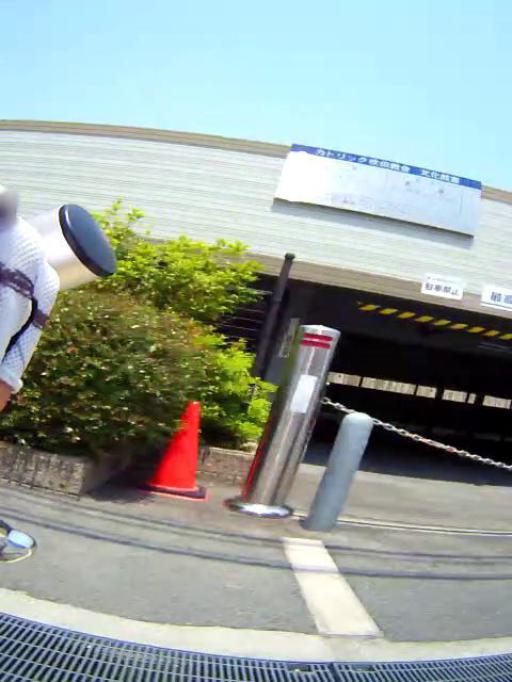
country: JP
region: Osaka
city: Suita
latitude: 34.7627
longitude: 135.5150
